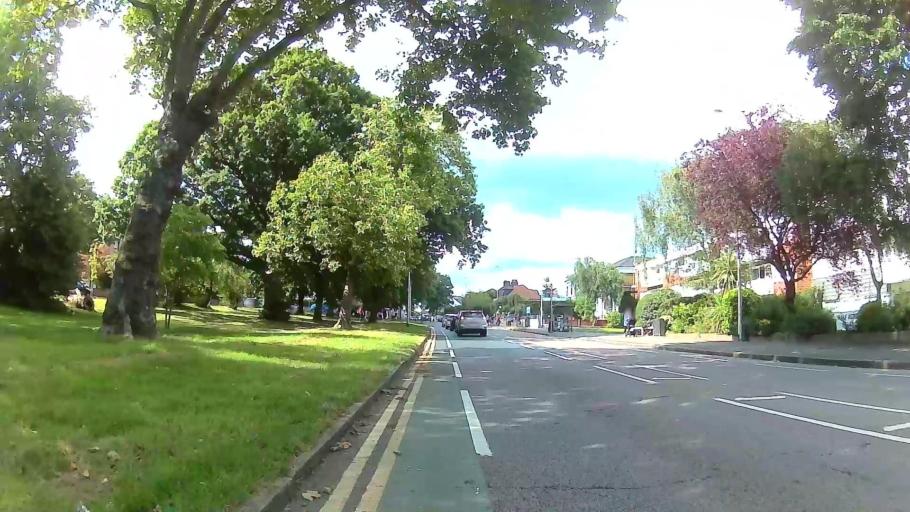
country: GB
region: England
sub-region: Greater London
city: Woodford Green
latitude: 51.5910
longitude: 0.0224
